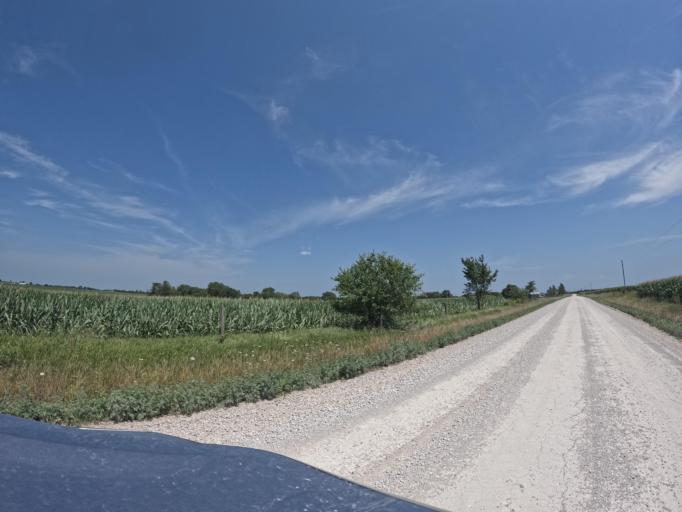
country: US
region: Iowa
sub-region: Henry County
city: Mount Pleasant
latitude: 40.9267
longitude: -91.6518
